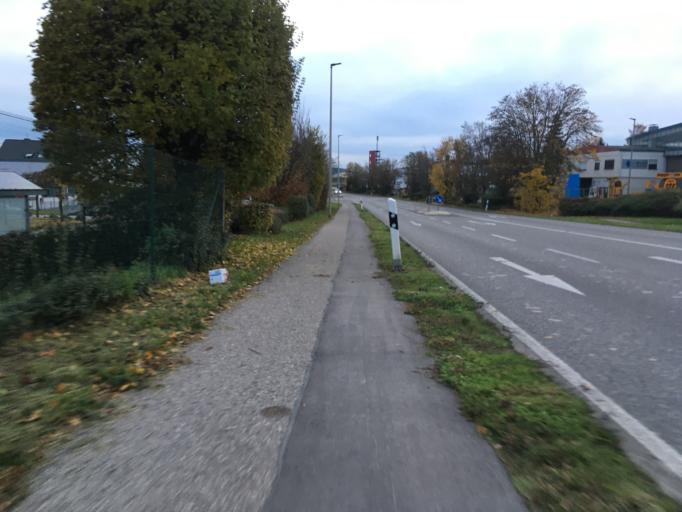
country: DE
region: Baden-Wuerttemberg
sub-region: Regierungsbezirk Stuttgart
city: Abstatt
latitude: 49.0775
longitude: 9.2907
